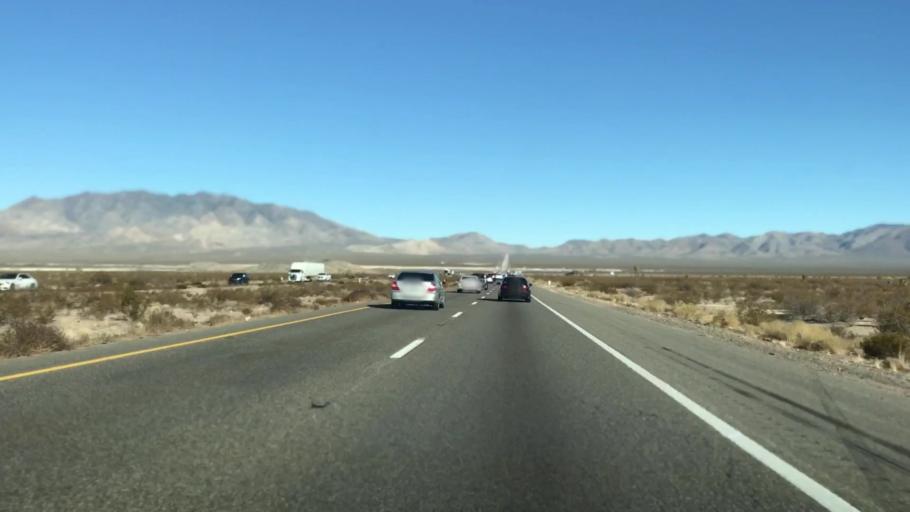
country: US
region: Nevada
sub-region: Clark County
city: Sandy Valley
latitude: 35.4284
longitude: -115.7173
